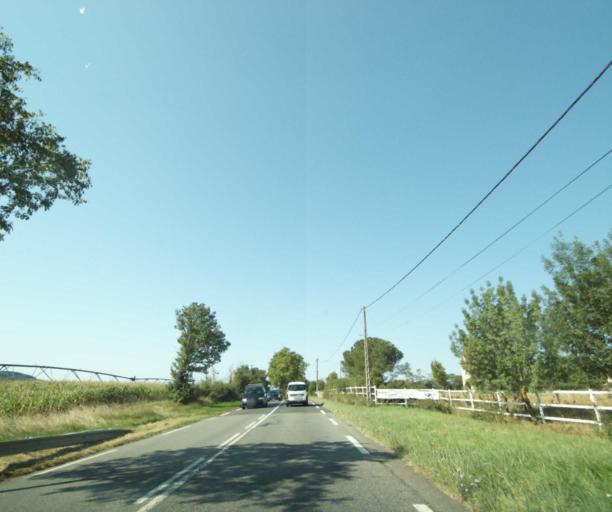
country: FR
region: Midi-Pyrenees
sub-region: Departement de la Haute-Garonne
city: Beaumont-sur-Leze
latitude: 43.4018
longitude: 1.3661
